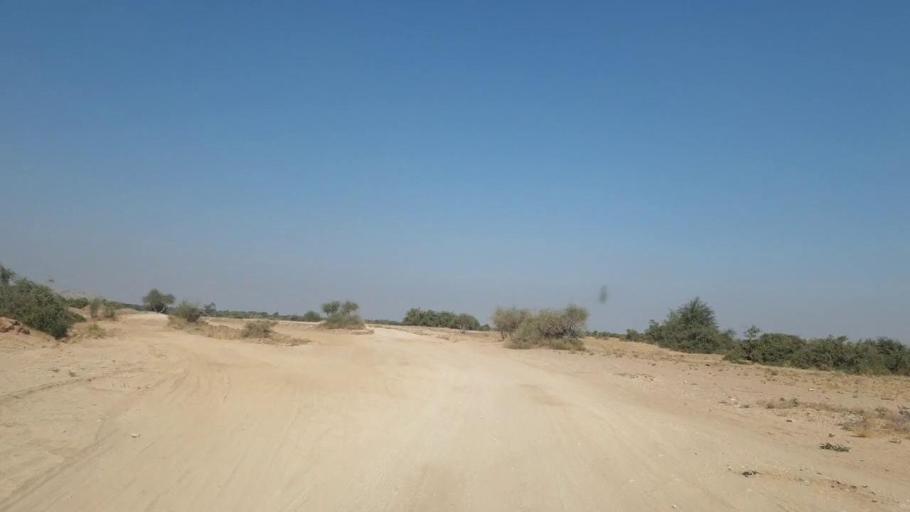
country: PK
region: Sindh
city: Jamshoro
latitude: 25.2773
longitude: 67.8074
